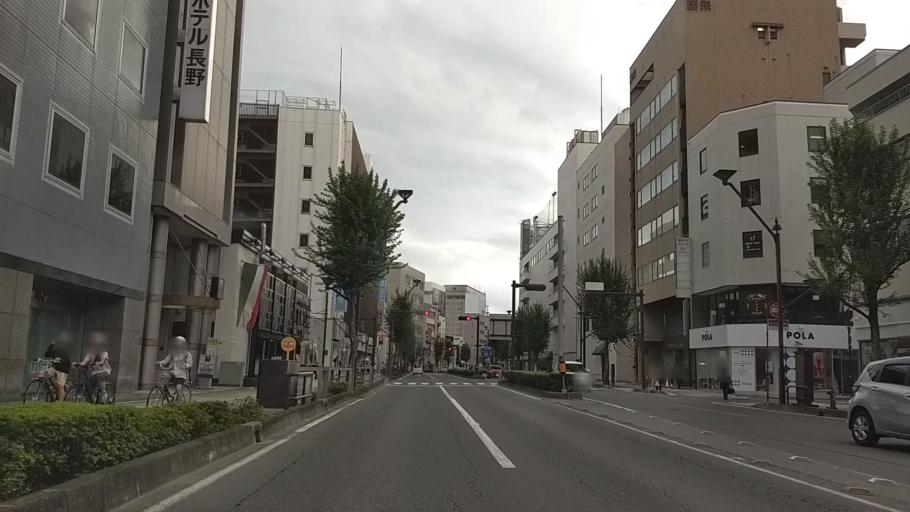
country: JP
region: Nagano
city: Nagano-shi
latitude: 36.6461
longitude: 138.1903
